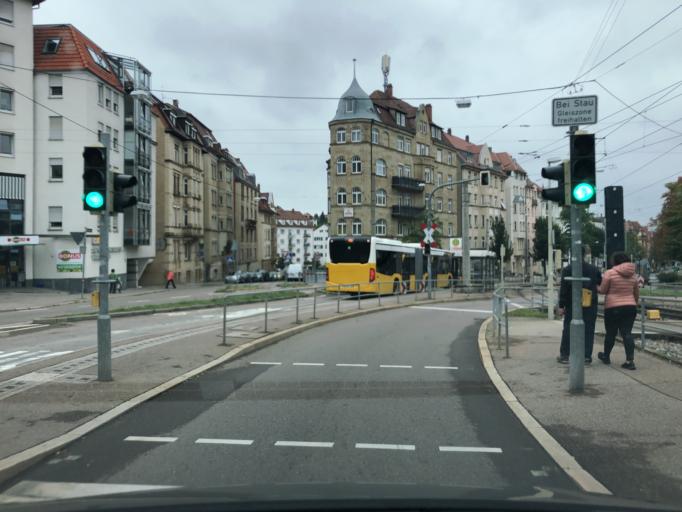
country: DE
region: Baden-Wuerttemberg
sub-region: Regierungsbezirk Stuttgart
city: Stuttgart
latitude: 48.7745
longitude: 9.1444
